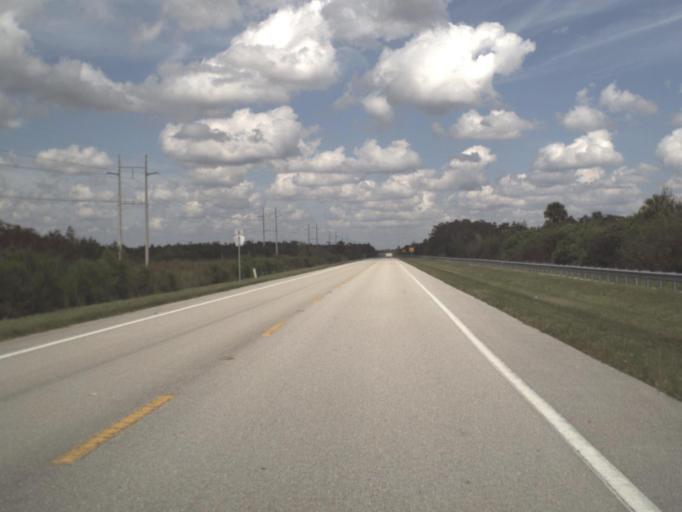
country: US
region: Florida
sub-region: Collier County
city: Lely Resort
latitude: 25.9655
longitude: -81.3534
